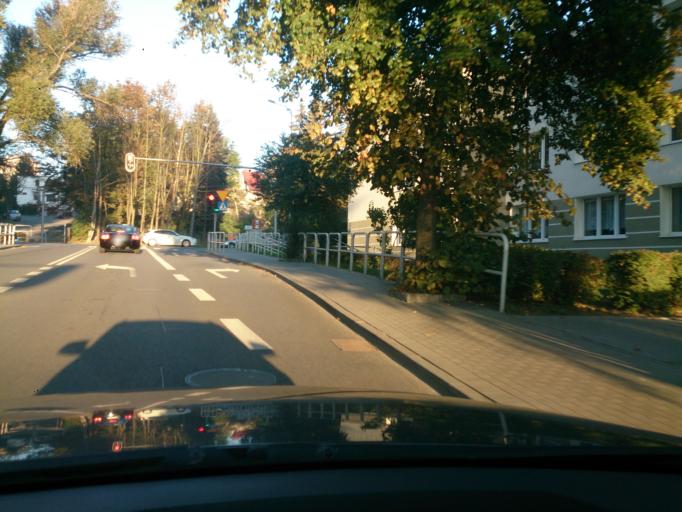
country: PL
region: Pomeranian Voivodeship
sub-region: Gdynia
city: Gdynia
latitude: 54.4926
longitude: 18.5412
